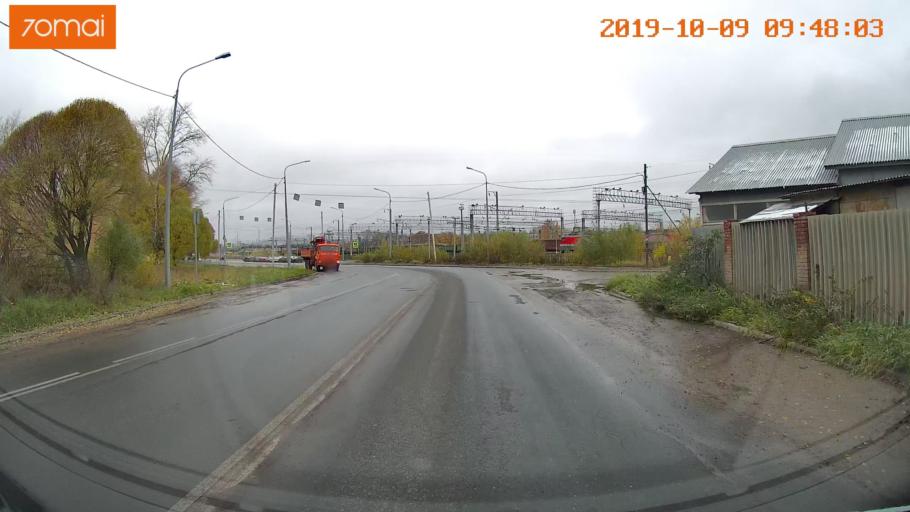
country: RU
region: Vologda
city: Vologda
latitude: 59.1928
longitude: 39.9338
